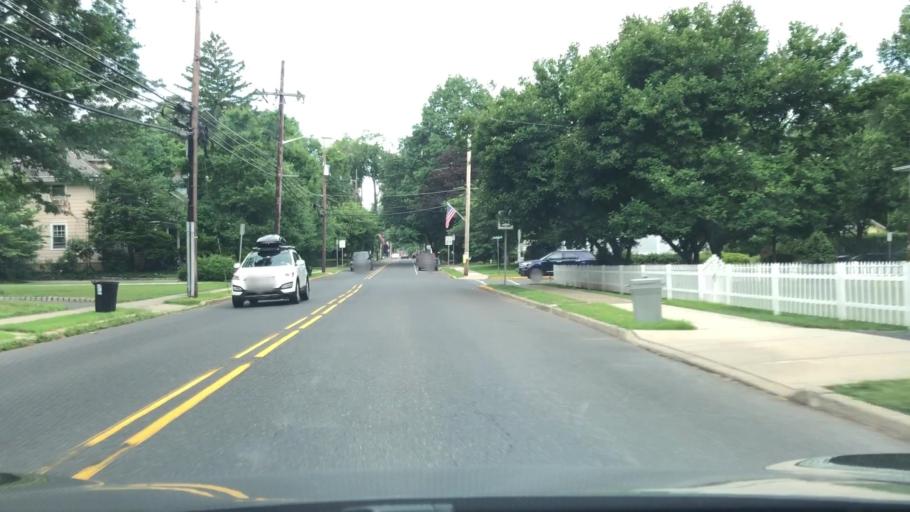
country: US
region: New Jersey
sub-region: Mercer County
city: Pennington
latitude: 40.3283
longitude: -74.7880
